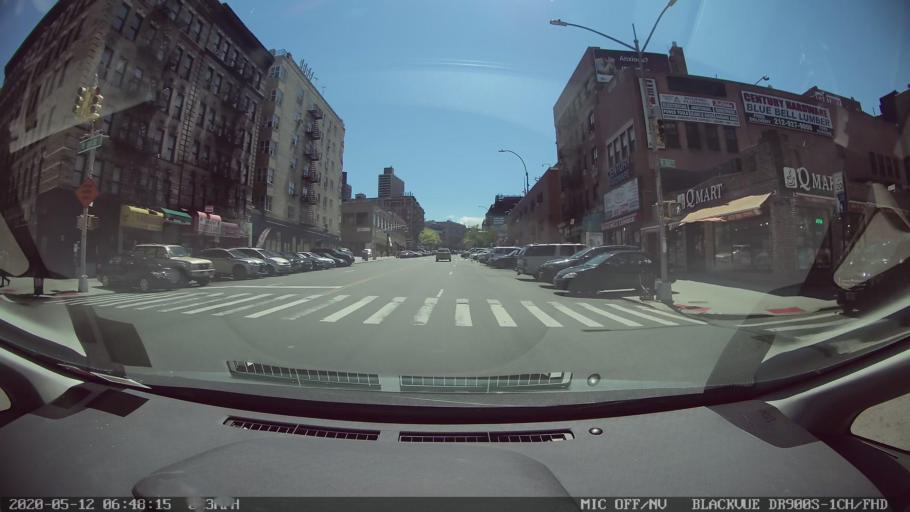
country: US
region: New York
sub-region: New York County
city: Inwood
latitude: 40.8521
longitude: -73.9349
